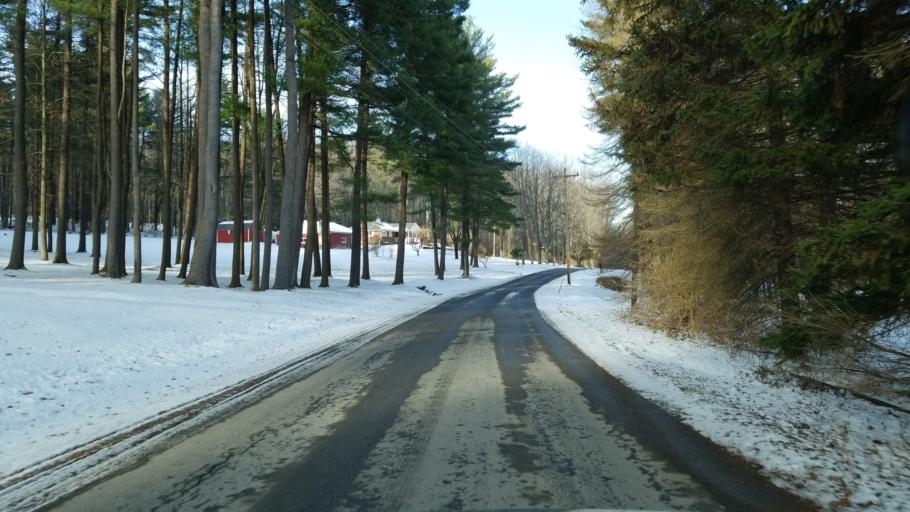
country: US
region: Pennsylvania
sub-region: Clearfield County
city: Treasure Lake
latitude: 41.0940
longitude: -78.6377
